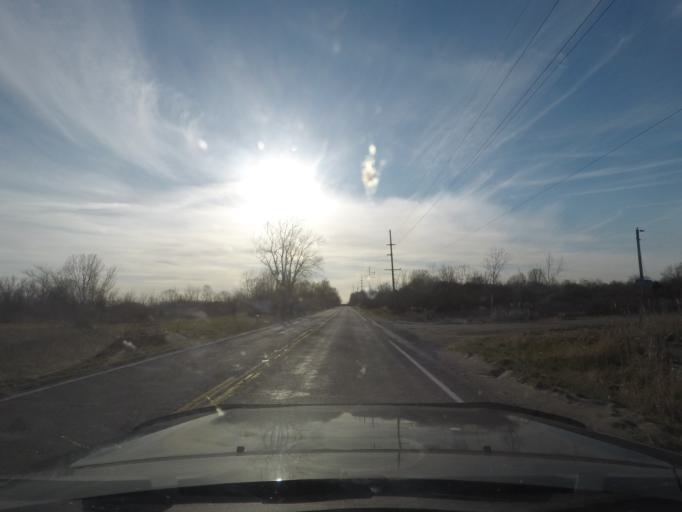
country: US
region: Indiana
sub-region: Saint Joseph County
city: Walkerton
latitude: 41.4481
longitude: -86.4130
